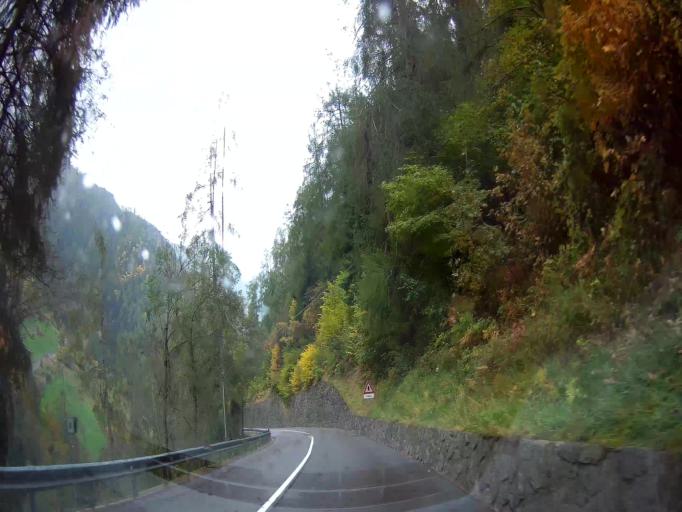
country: IT
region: Trentino-Alto Adige
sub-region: Bolzano
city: Certosa
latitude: 46.7061
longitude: 10.9125
